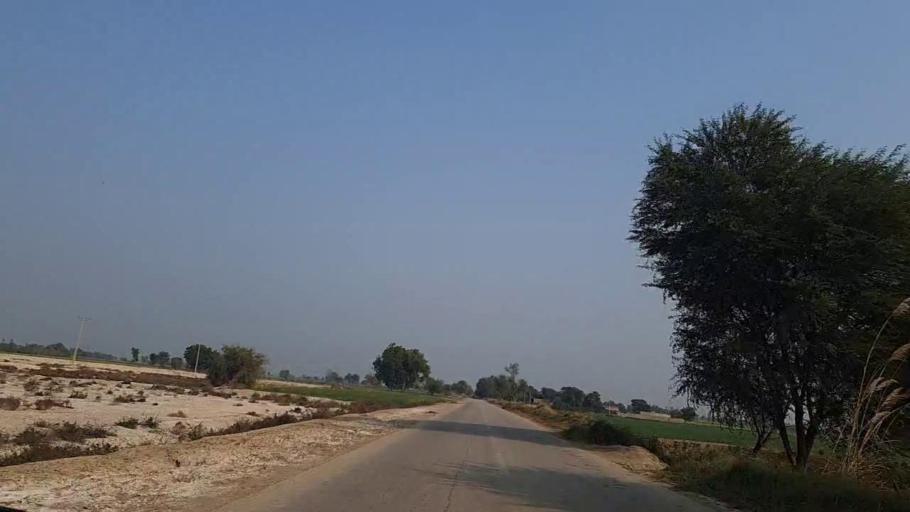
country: PK
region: Sindh
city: Sakrand
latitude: 26.1336
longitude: 68.2025
